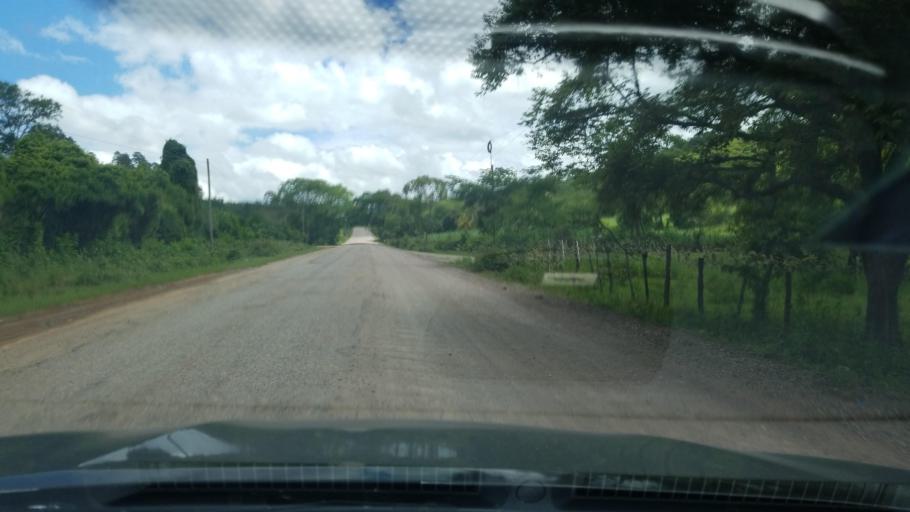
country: HN
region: Francisco Morazan
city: Talanga
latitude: 14.3817
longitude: -87.0682
